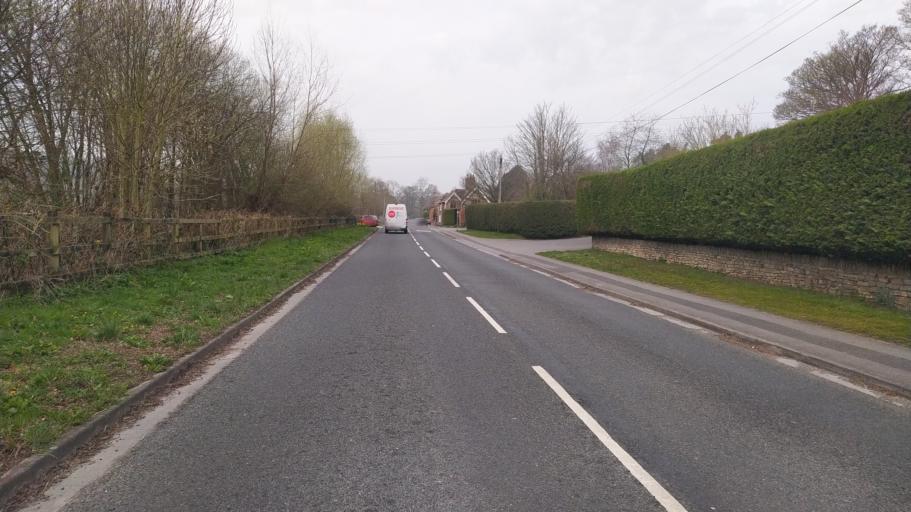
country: GB
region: England
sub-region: Dorset
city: Dorchester
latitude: 50.7516
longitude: -2.5227
